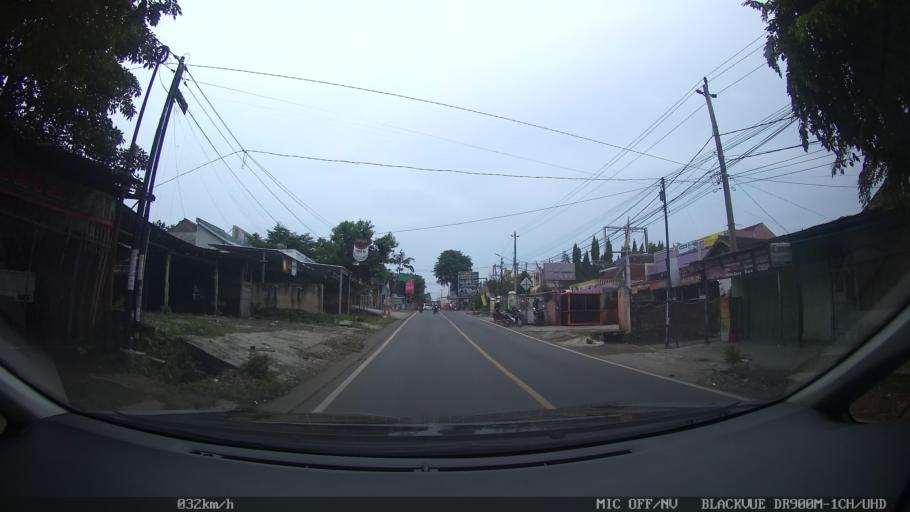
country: ID
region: Lampung
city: Kedaton
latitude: -5.3935
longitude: 105.2309
